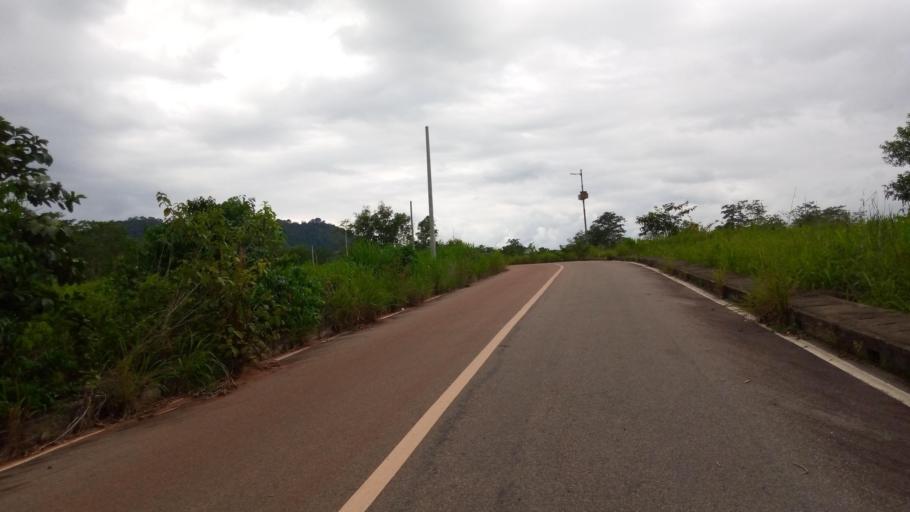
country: SL
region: Southern Province
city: Moyamba
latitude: 8.1603
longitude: -12.4432
